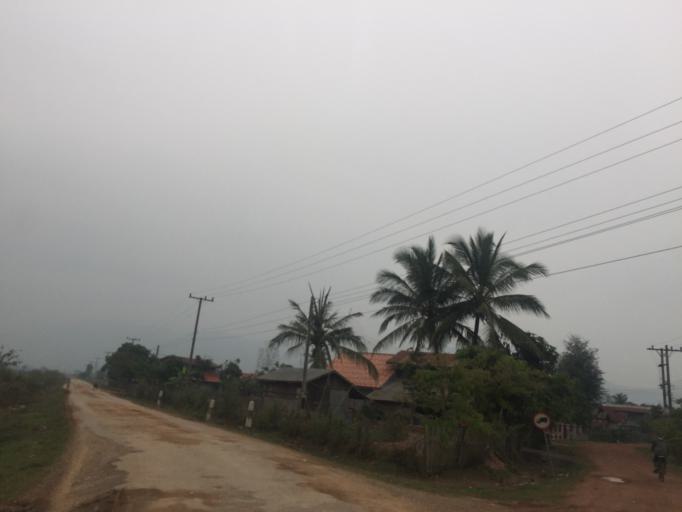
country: LA
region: Xiagnabouli
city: Sainyabuli
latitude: 18.9831
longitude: 101.5006
